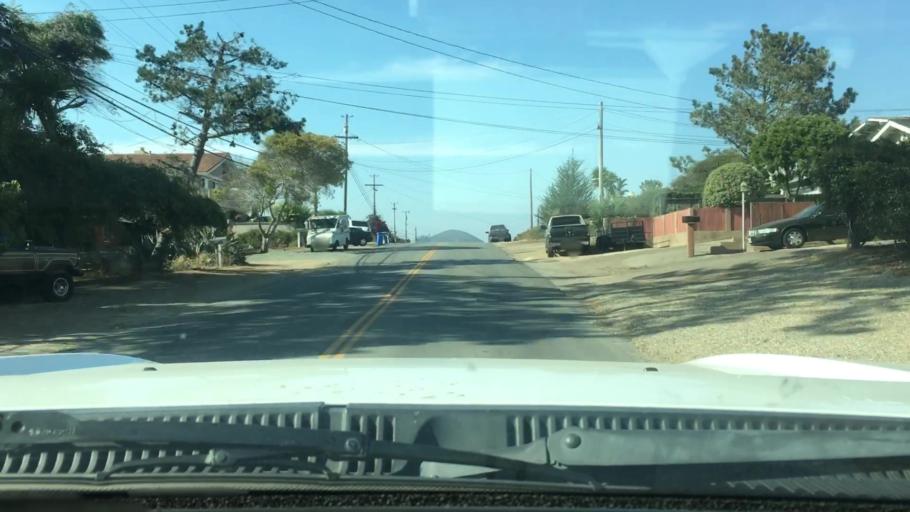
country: US
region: California
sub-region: San Luis Obispo County
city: Los Osos
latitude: 35.3212
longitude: -120.8311
